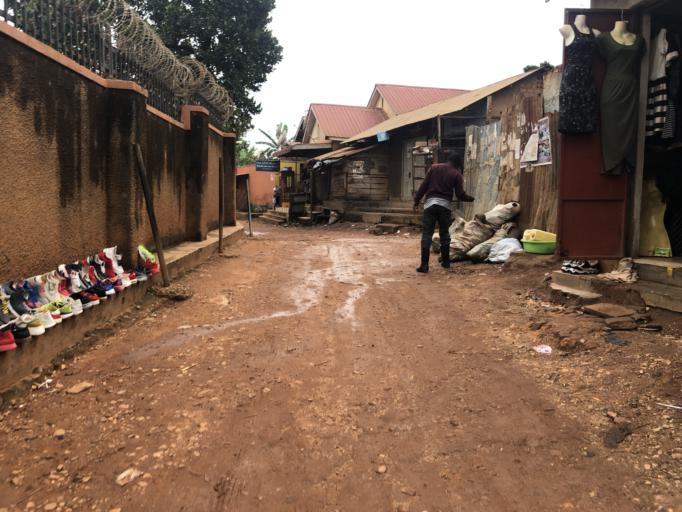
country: UG
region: Central Region
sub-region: Kampala District
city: Kampala
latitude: 0.2870
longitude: 32.6060
